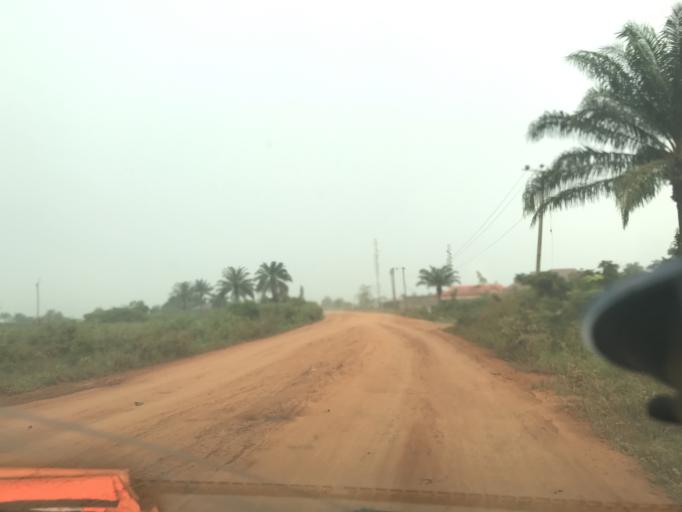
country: NG
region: Ogun
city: Ado Odo
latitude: 6.5664
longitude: 2.9427
